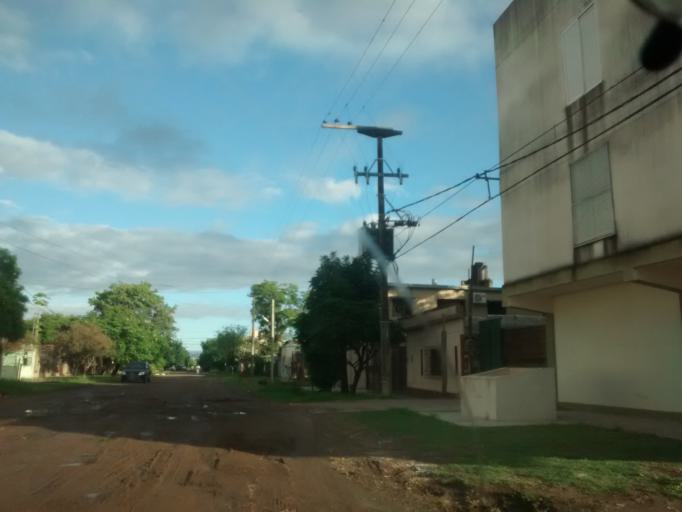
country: AR
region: Chaco
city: Resistencia
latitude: -27.4645
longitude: -58.9929
